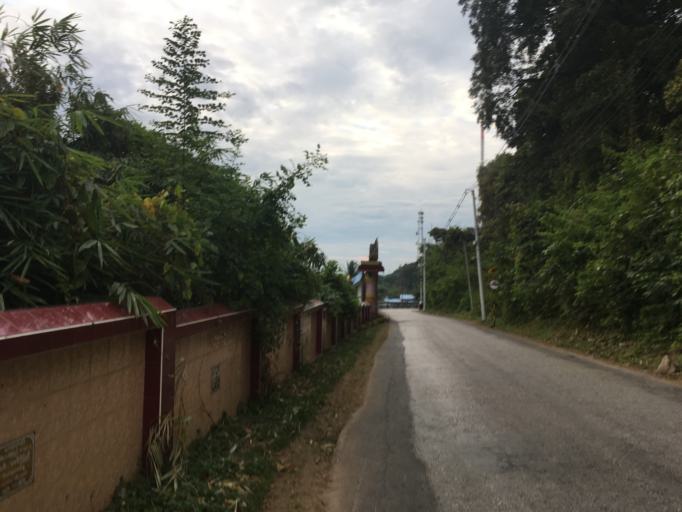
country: MM
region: Mon
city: Mawlamyine
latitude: 16.4713
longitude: 97.6308
